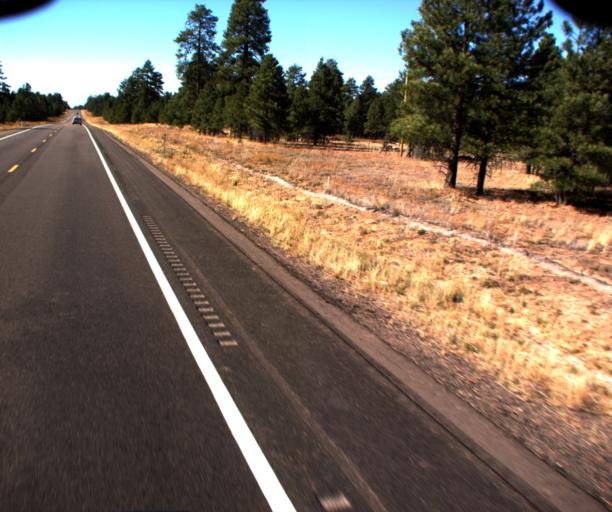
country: US
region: Arizona
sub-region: Apache County
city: Saint Michaels
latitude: 35.6905
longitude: -109.2555
